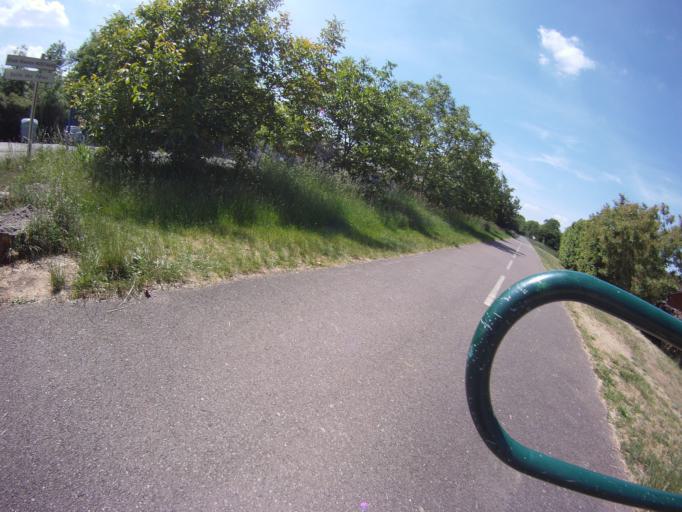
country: FR
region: Lorraine
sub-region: Departement de Meurthe-et-Moselle
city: Lay-Saint-Christophe
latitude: 48.7459
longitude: 6.2051
